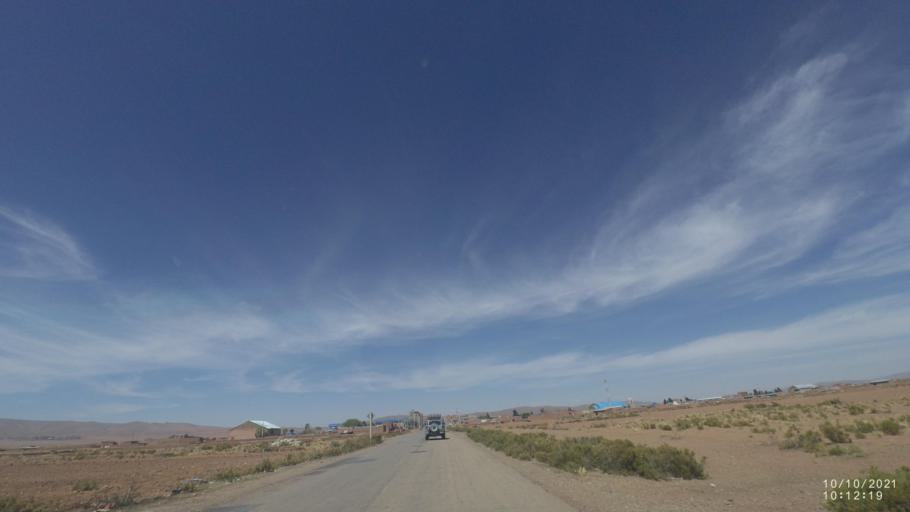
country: BO
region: La Paz
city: Eucaliptus
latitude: -17.4337
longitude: -67.5137
